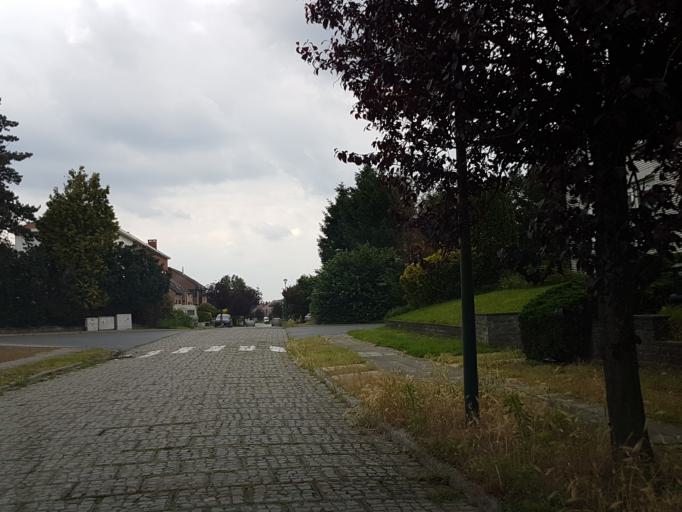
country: BE
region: Flanders
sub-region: Provincie Vlaams-Brabant
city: Kraainem
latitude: 50.8671
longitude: 4.4422
